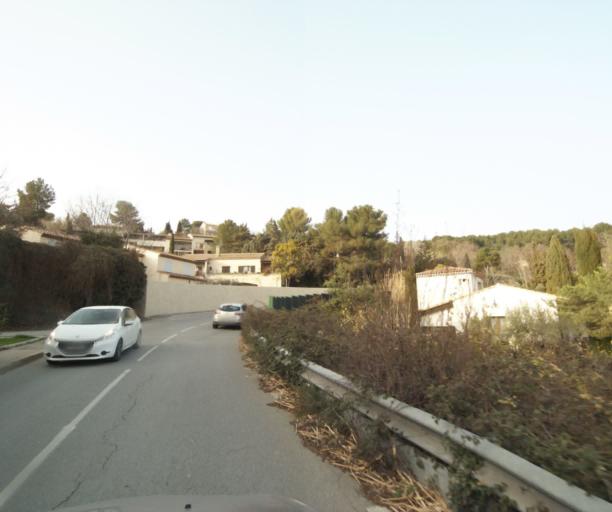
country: FR
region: Provence-Alpes-Cote d'Azur
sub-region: Departement des Bouches-du-Rhone
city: Eguilles
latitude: 43.5675
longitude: 5.3596
